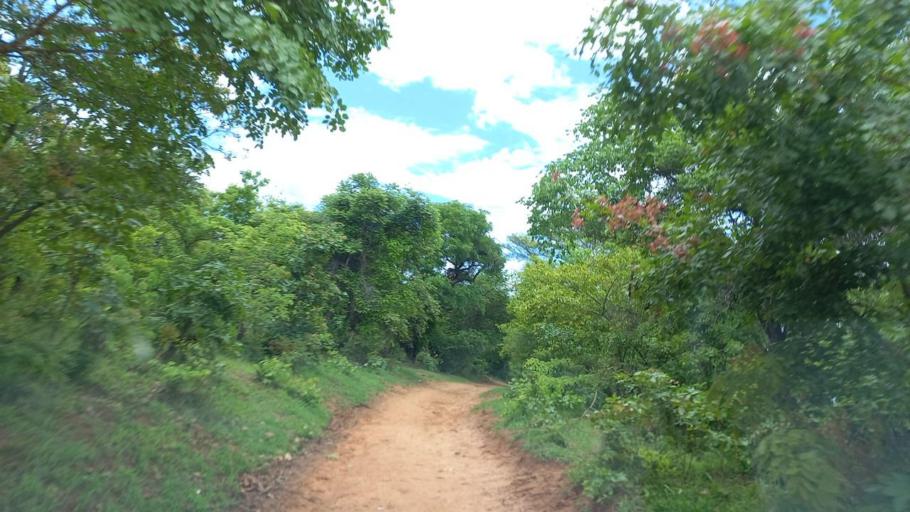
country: ZM
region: North-Western
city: Kabompo
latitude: -13.6090
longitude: 24.2487
